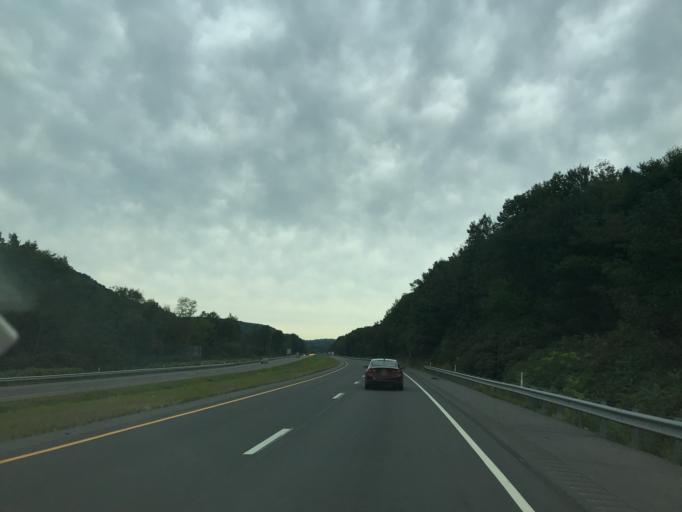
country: US
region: Pennsylvania
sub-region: Wyoming County
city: Factoryville
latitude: 41.7422
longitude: -75.6770
